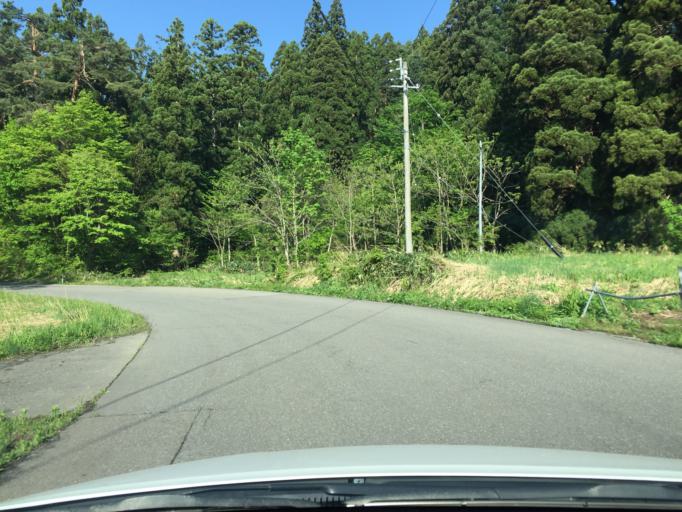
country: JP
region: Fukushima
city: Kitakata
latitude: 37.6844
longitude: 139.6930
